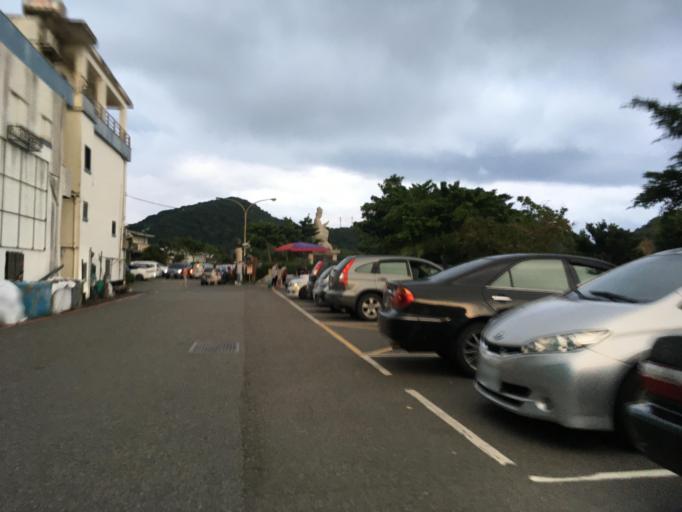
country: TW
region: Taiwan
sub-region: Yilan
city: Yilan
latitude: 24.5773
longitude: 121.8698
